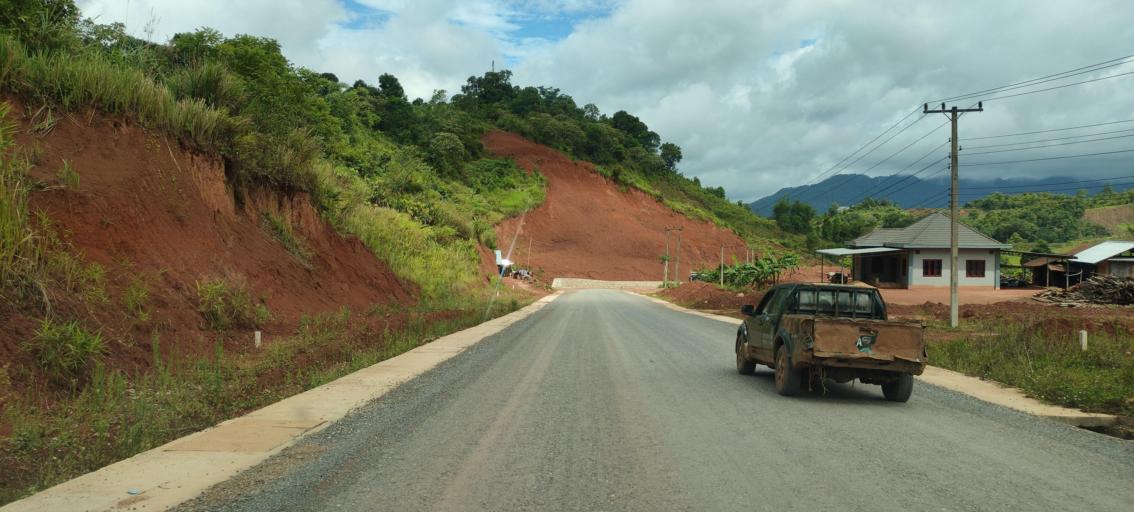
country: LA
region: Phongsali
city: Phongsali
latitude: 21.6351
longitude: 101.9210
